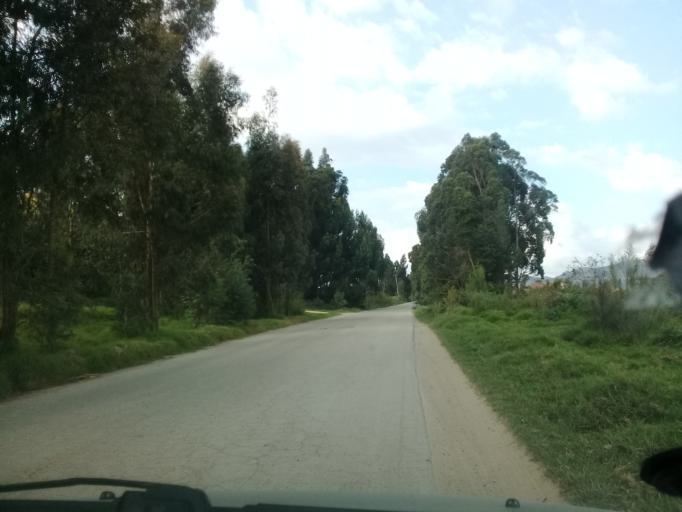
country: CO
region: Cundinamarca
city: Funza
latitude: 4.7744
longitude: -74.2211
